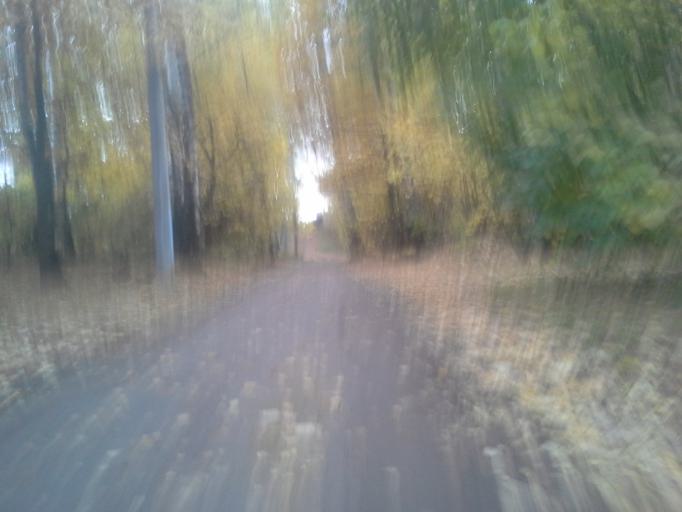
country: RU
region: Moscow
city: Novo-Peredelkino
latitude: 55.6506
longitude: 37.3333
